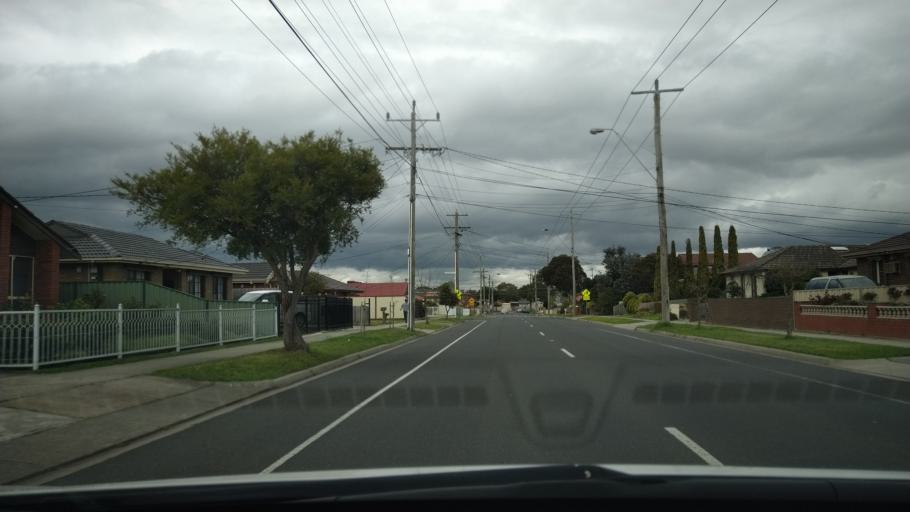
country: AU
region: Victoria
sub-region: Greater Dandenong
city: Springvale South
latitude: -37.9793
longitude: 145.1535
